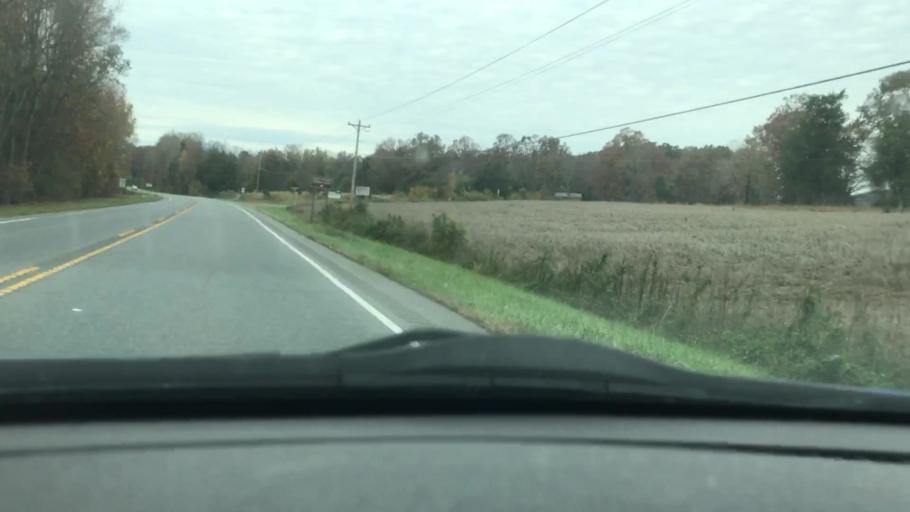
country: US
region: North Carolina
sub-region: Randolph County
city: Asheboro
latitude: 35.7309
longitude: -79.9432
